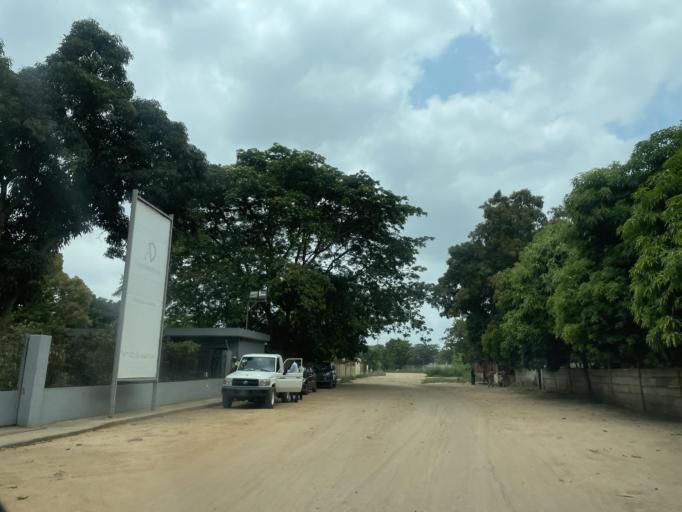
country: AO
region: Luanda
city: Luanda
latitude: -8.9117
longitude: 13.3773
